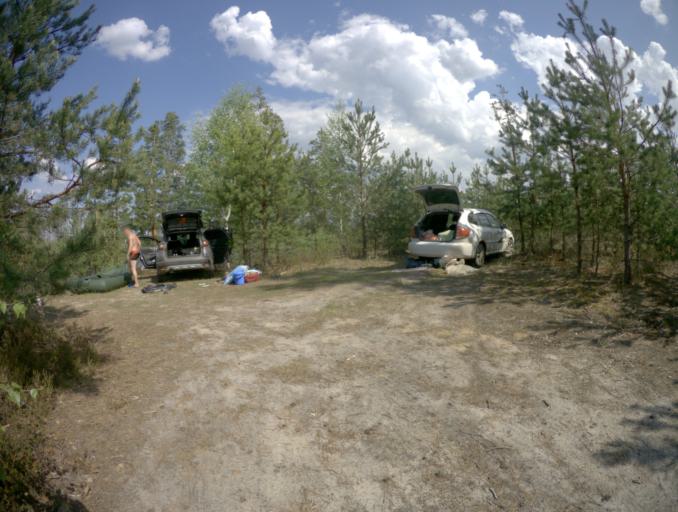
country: RU
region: Ivanovo
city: Talitsy
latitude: 56.4677
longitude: 42.1945
